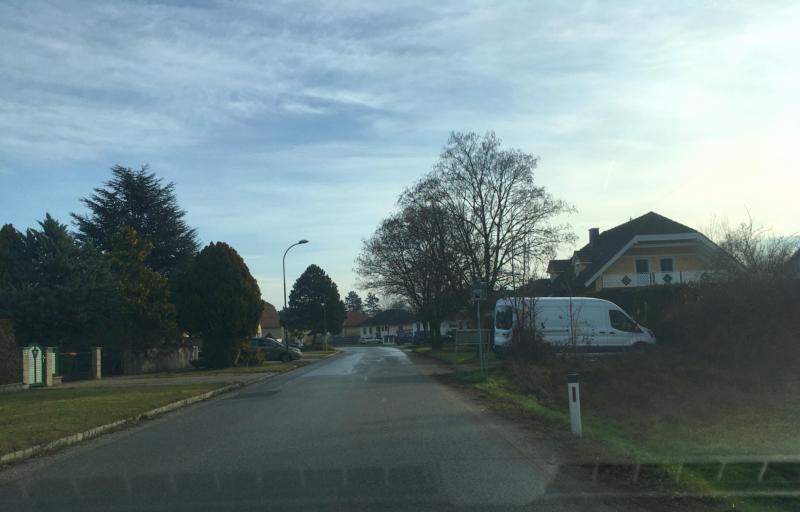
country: AT
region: Lower Austria
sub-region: Politischer Bezirk Ganserndorf
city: Leopoldsdorf im Marchfelde
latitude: 48.1936
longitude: 16.7029
